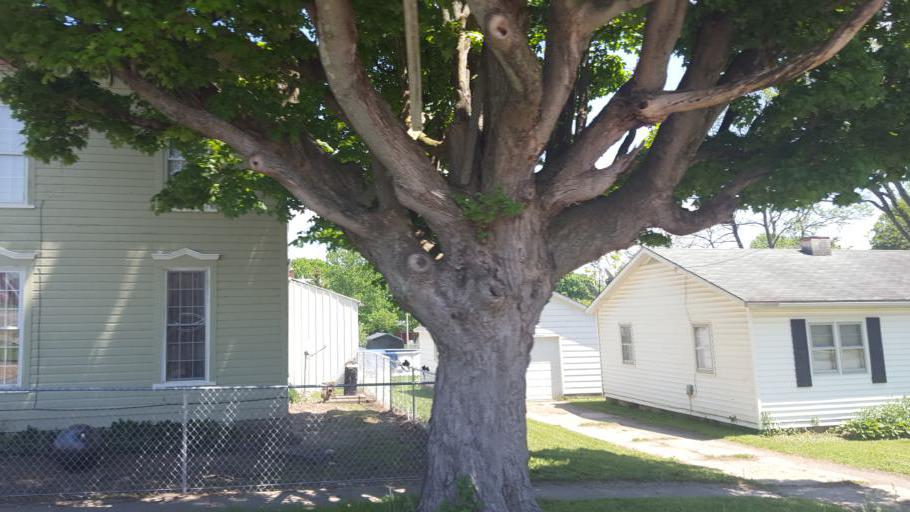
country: US
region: Ohio
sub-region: Knox County
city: Oak Hill
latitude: 40.2844
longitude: -82.2839
